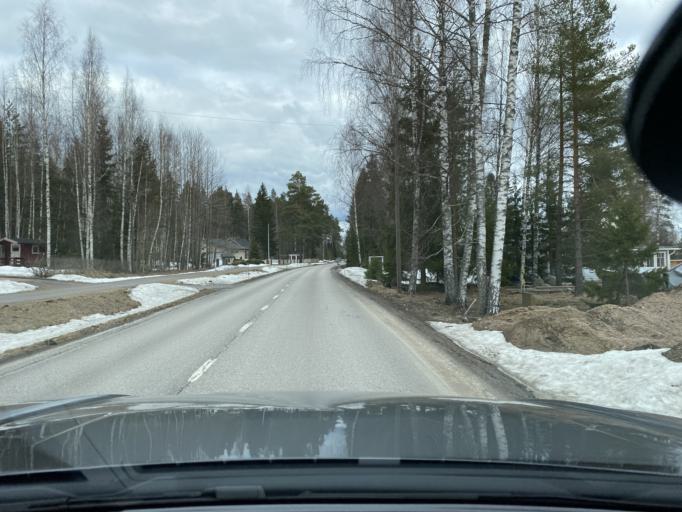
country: FI
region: Uusimaa
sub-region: Helsinki
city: Hyvinge
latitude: 60.5832
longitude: 24.7925
